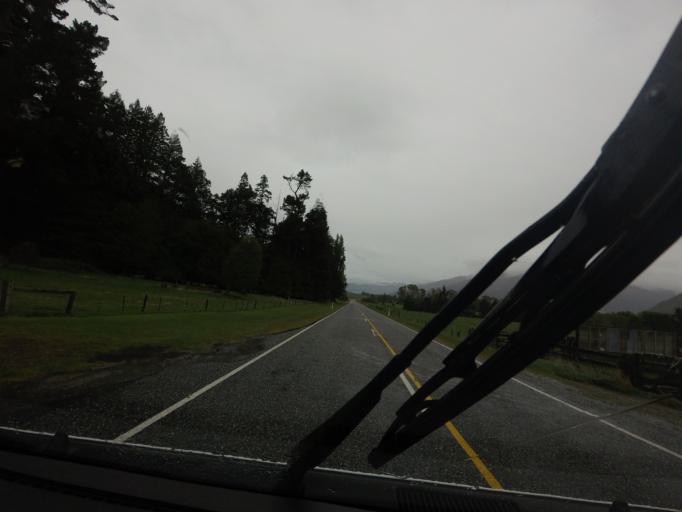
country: NZ
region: Otago
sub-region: Queenstown-Lakes District
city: Wanaka
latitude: -44.2470
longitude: 169.2217
